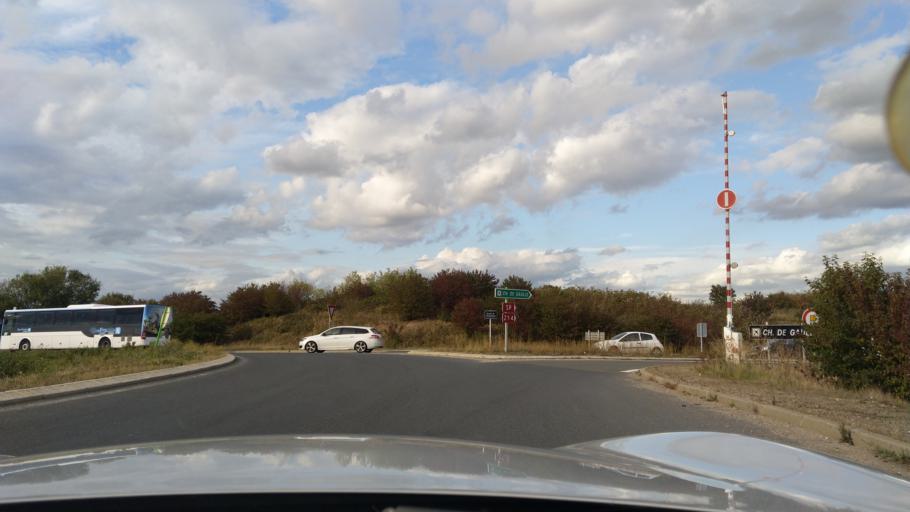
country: FR
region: Ile-de-France
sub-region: Departement du Val-d'Oise
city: Roissy-en-France
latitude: 49.0273
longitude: 2.5337
